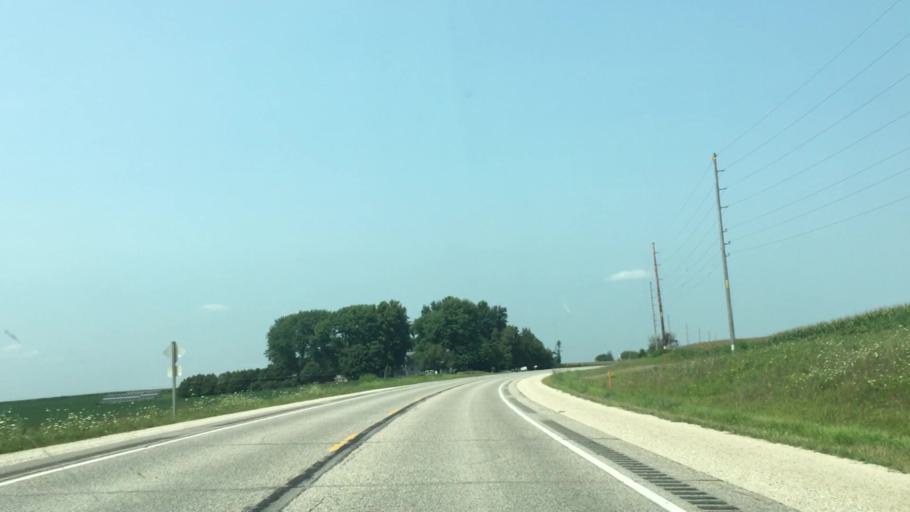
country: US
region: Iowa
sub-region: Fayette County
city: West Union
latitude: 42.9099
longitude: -91.8139
